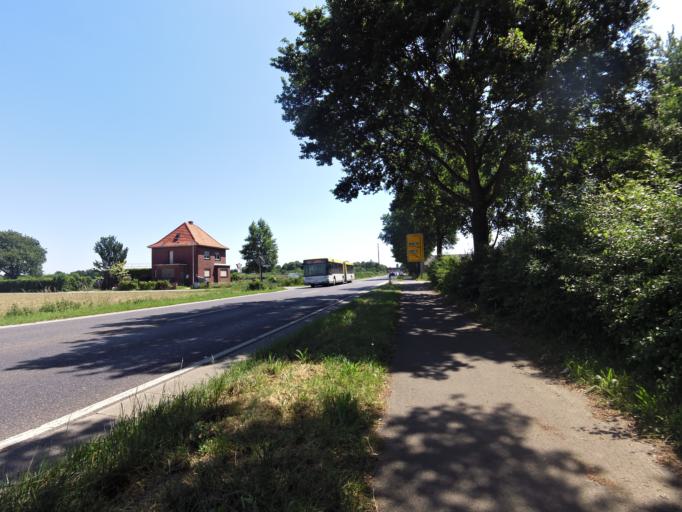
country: DE
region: North Rhine-Westphalia
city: Geilenkirchen
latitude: 50.9752
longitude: 6.0861
